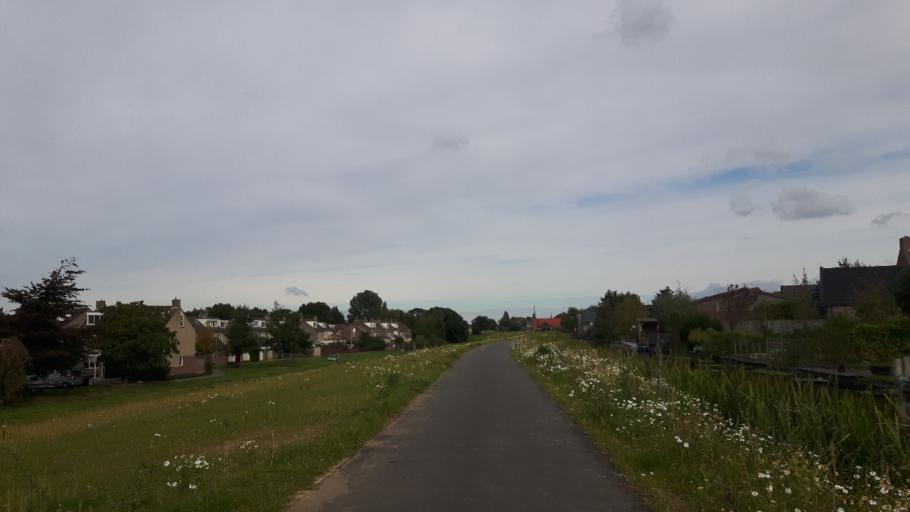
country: NL
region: South Holland
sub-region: Gemeente Nieuwkoop
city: Nieuwkoop
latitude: 52.1415
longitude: 4.7690
